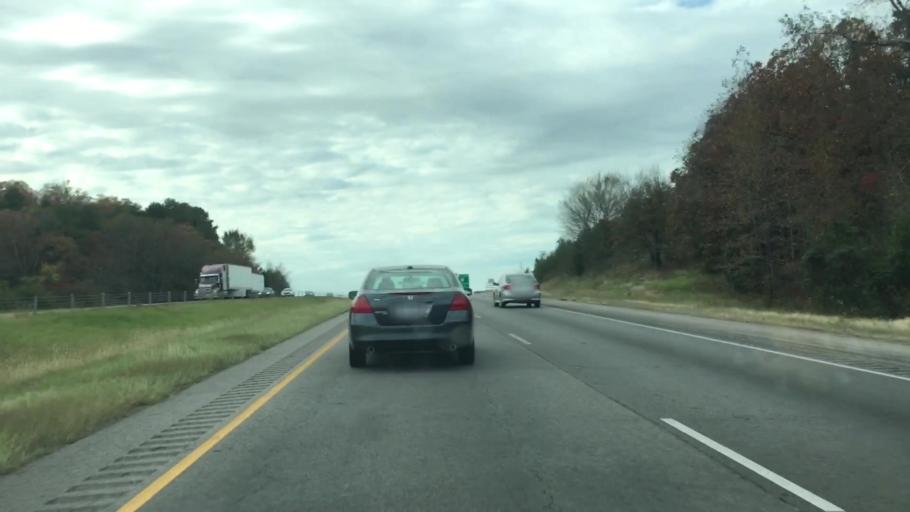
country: US
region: Arkansas
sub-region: Conway County
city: Morrilton
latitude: 35.1699
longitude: -92.6935
